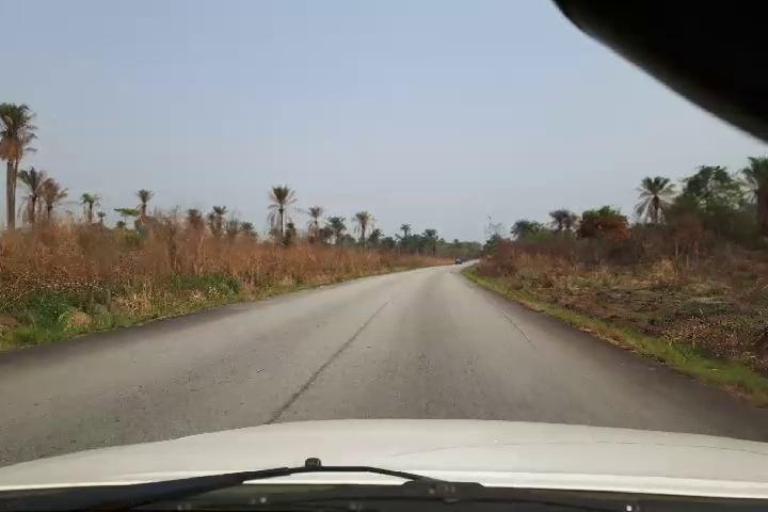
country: SL
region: Southern Province
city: Baiima
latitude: 8.1381
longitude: -11.8966
